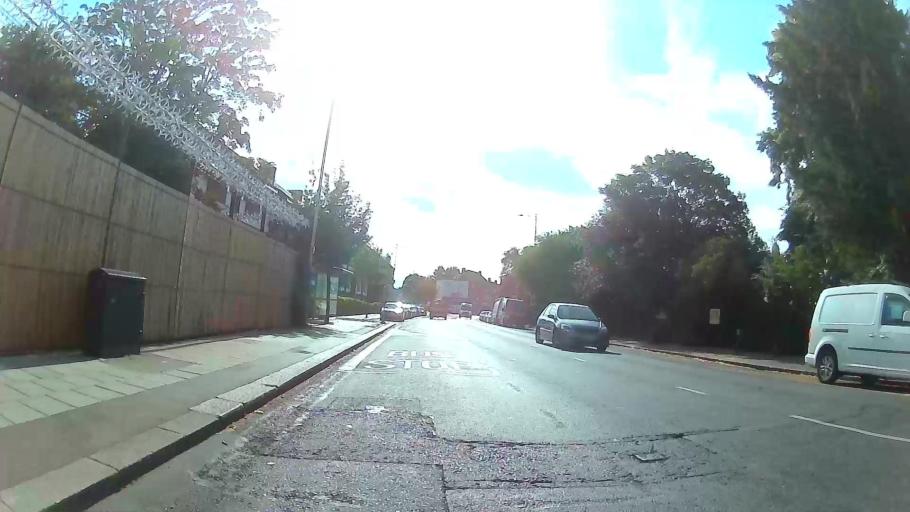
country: GB
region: England
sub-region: Greater London
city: Becontree
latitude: 51.5632
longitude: 0.1173
